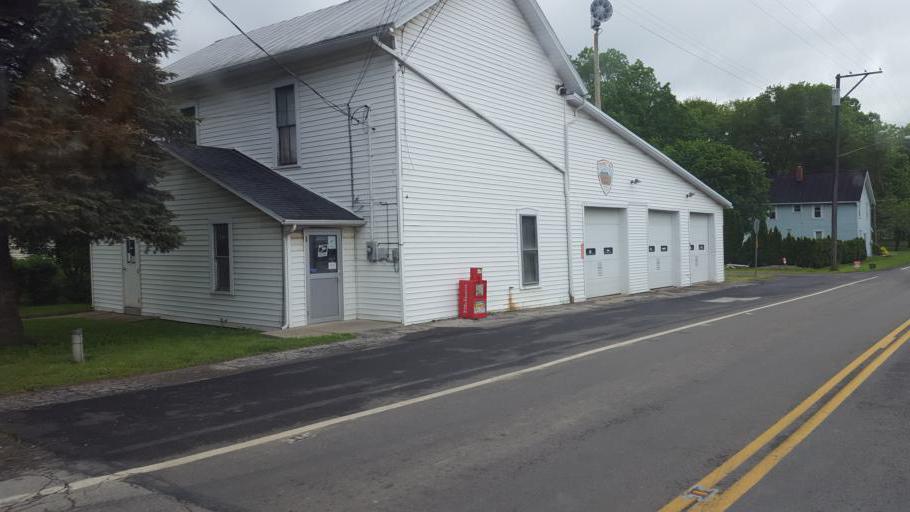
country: US
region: Ohio
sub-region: Ashland County
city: Ashland
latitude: 40.9217
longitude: -82.2815
